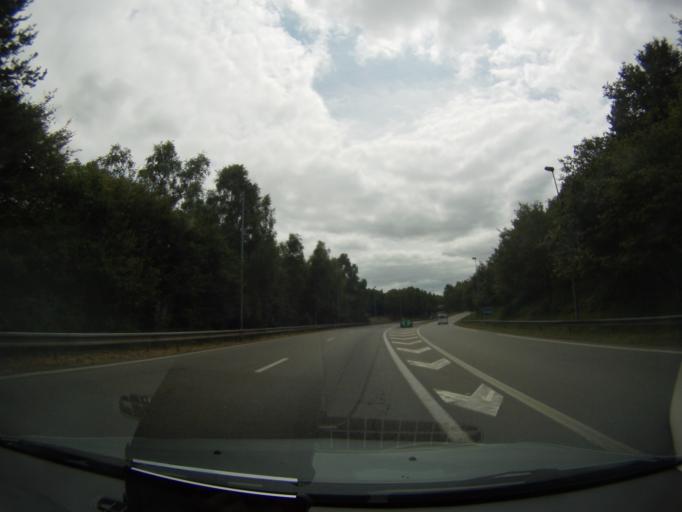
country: FR
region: Pays de la Loire
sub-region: Departement de la Loire-Atlantique
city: La Chapelle-sur-Erdre
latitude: 47.2621
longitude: -1.5572
